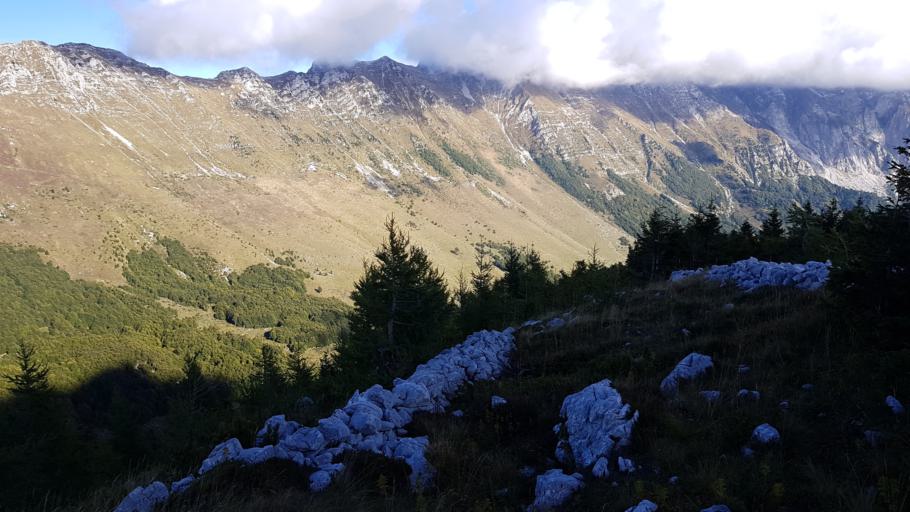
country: SI
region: Kobarid
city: Kobarid
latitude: 46.2913
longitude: 13.6055
